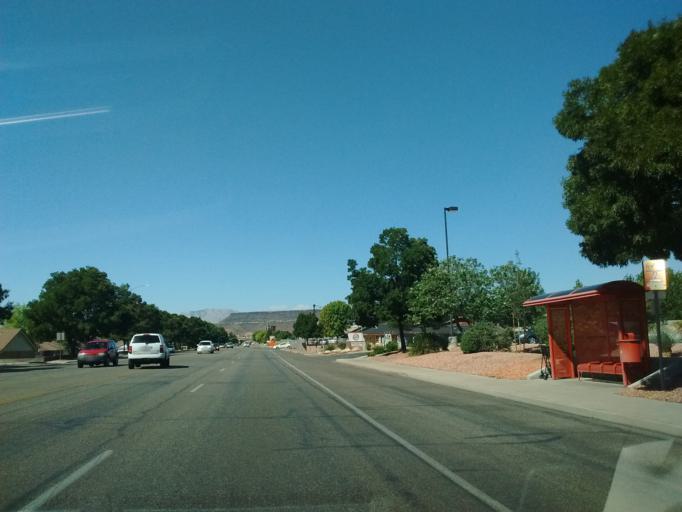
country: US
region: Utah
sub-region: Washington County
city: Saint George
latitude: 37.0963
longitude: -113.5584
